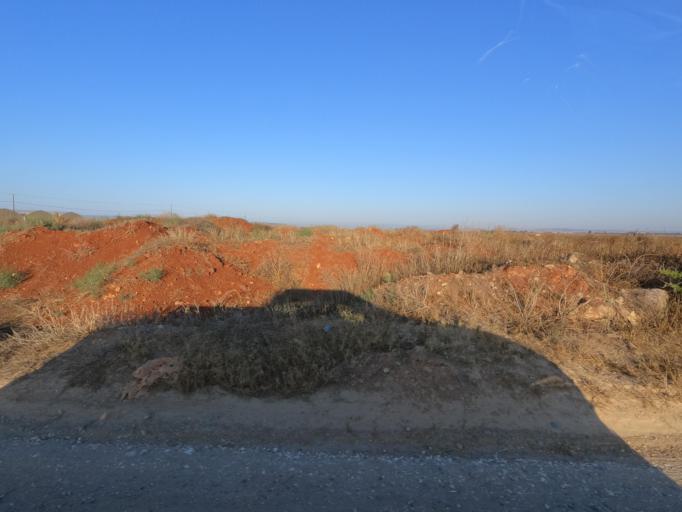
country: CY
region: Ammochostos
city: Avgorou
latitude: 35.0110
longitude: 33.8037
